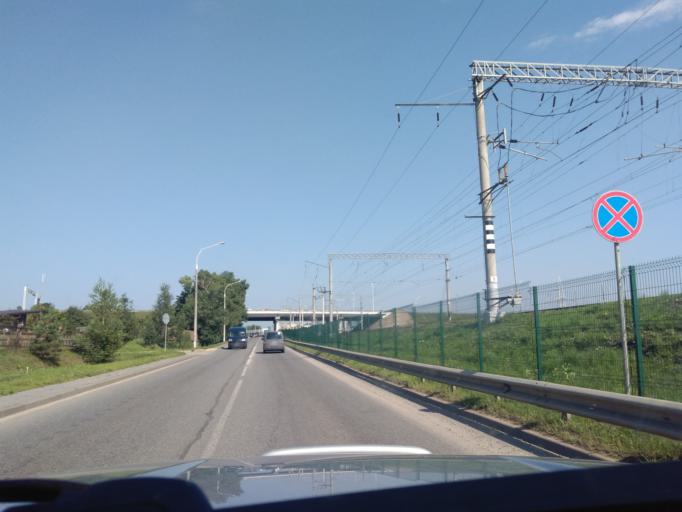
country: BY
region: Minsk
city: Zhdanovichy
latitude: 53.9412
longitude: 27.4368
